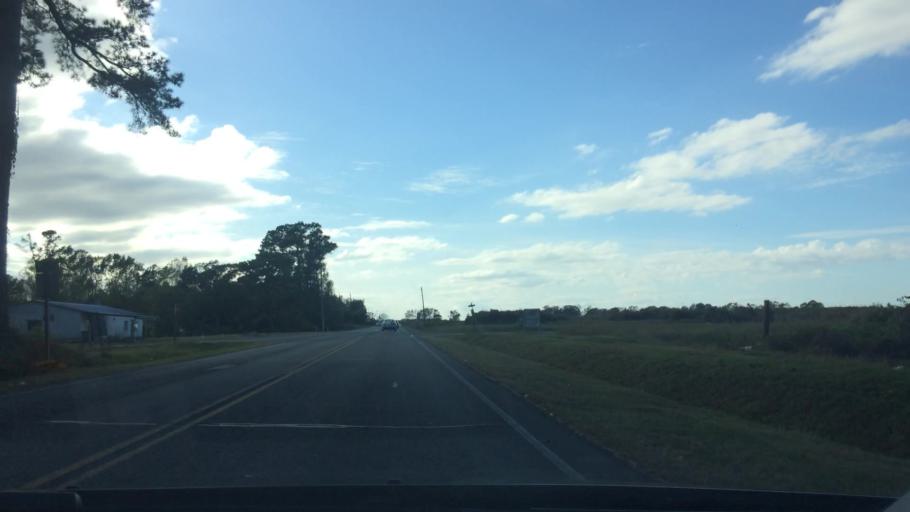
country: US
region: North Carolina
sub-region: Greene County
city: Snow Hill
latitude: 35.4382
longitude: -77.7594
